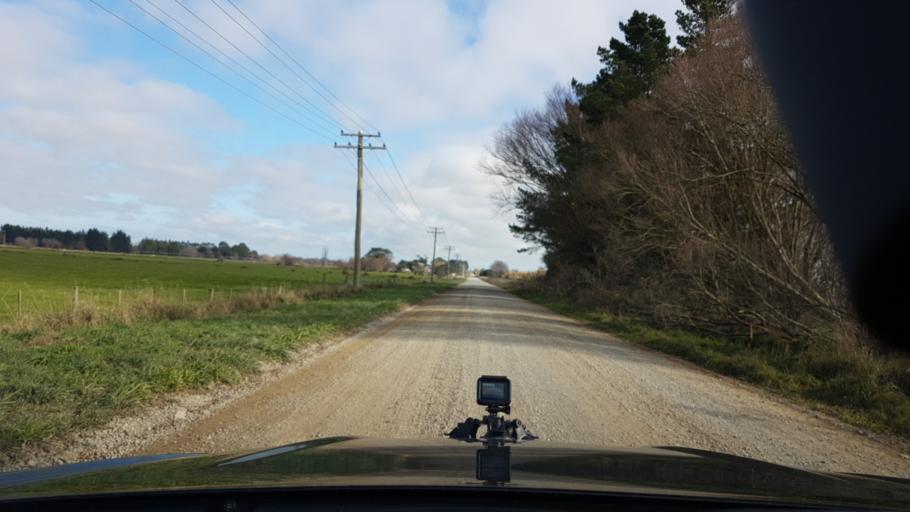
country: NZ
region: Canterbury
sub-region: Waimakariri District
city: Woodend
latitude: -43.3216
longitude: 172.6296
